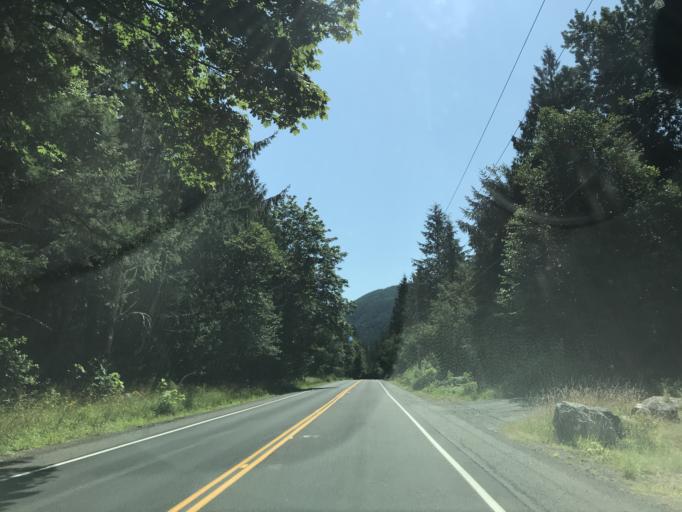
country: US
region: Washington
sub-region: King County
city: Ravensdale
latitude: 47.3575
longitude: -121.9044
